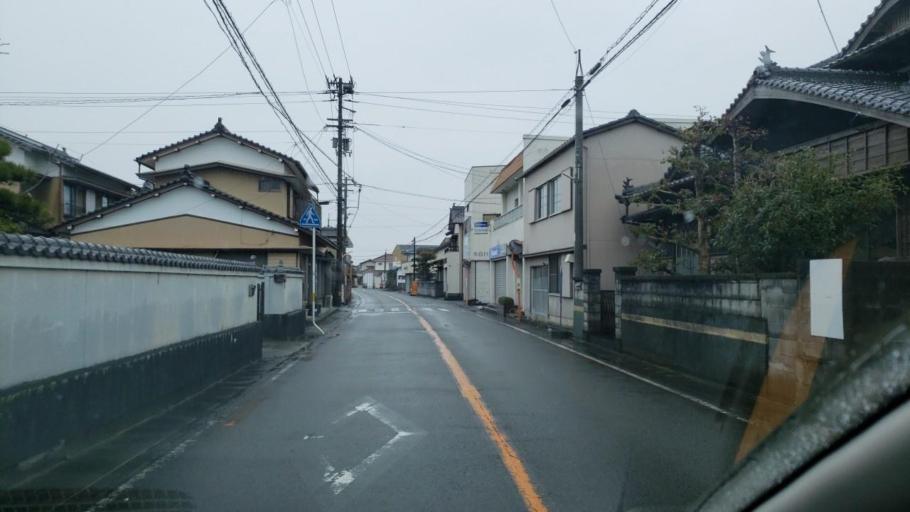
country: JP
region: Tokushima
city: Kamojimacho-jogejima
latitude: 34.0990
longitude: 134.3921
